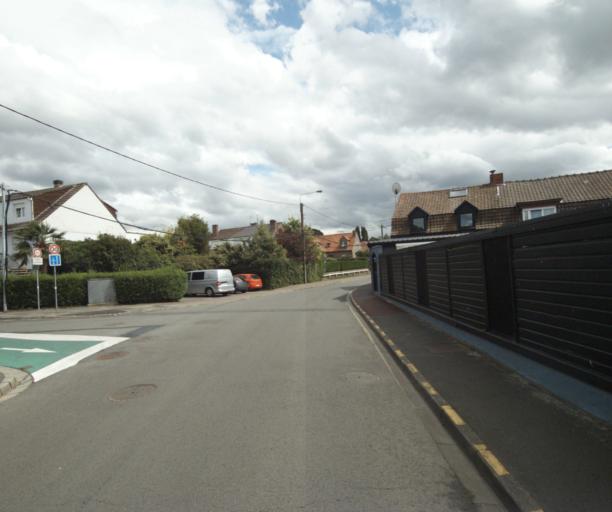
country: FR
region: Nord-Pas-de-Calais
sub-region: Departement du Nord
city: Roncq
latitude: 50.7535
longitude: 3.1159
